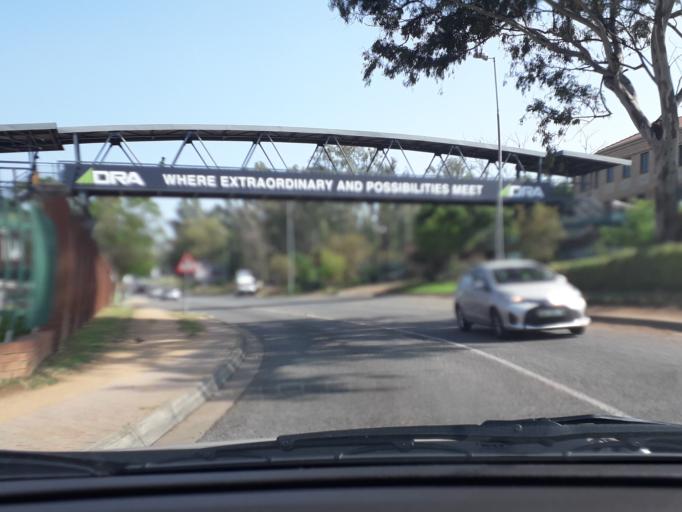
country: ZA
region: Gauteng
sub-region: City of Johannesburg Metropolitan Municipality
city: Midrand
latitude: -26.0382
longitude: 28.0665
